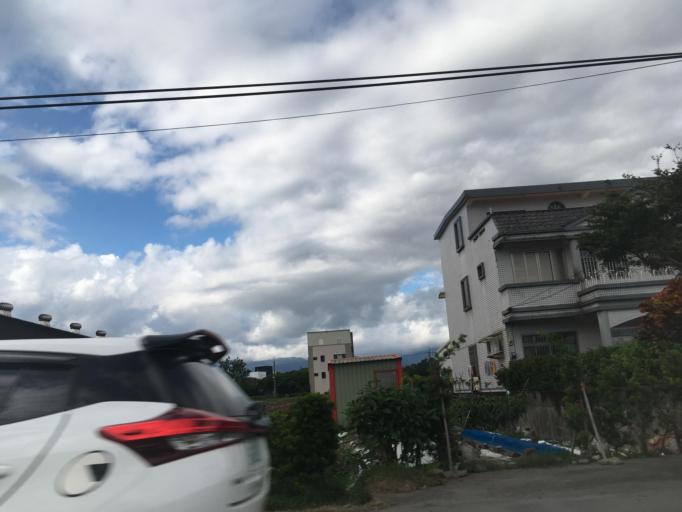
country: TW
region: Taiwan
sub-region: Yilan
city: Yilan
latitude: 24.6971
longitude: 121.7343
